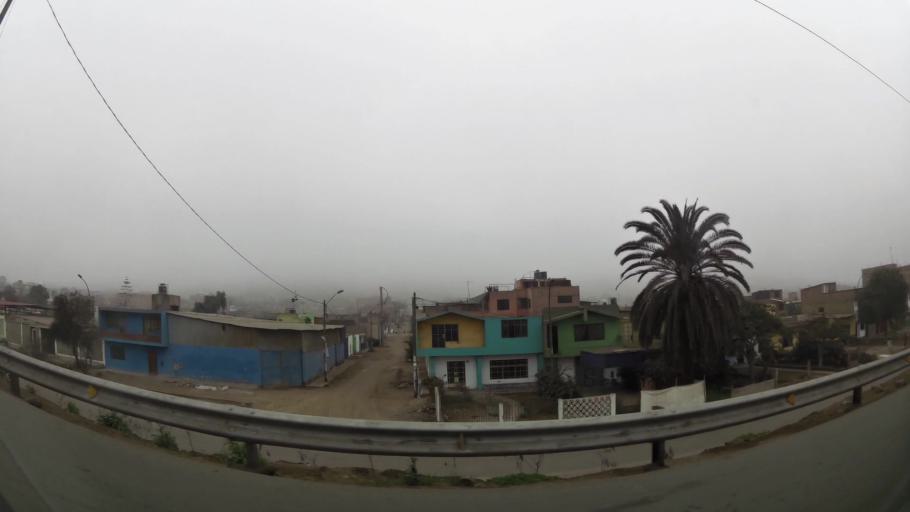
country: PE
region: Lima
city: Ventanilla
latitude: -11.8371
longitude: -77.1081
